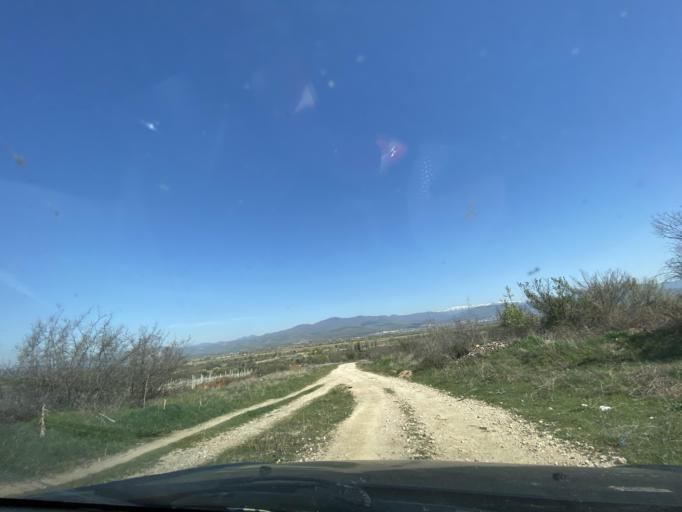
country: MK
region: Zrnovci
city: Zrnovci
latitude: 41.8510
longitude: 22.3896
